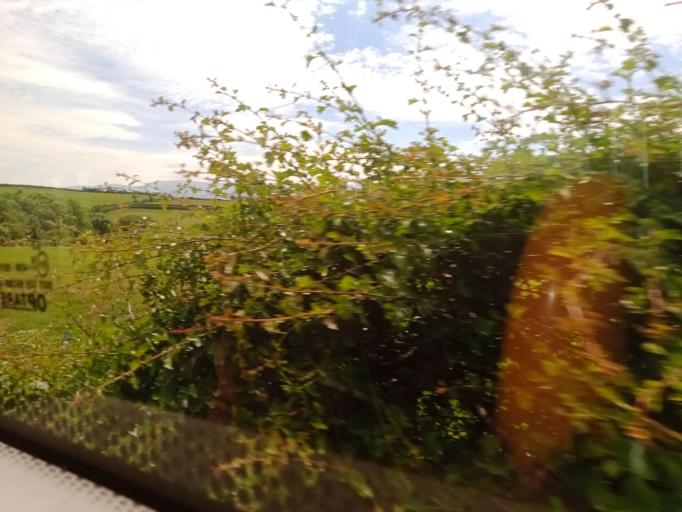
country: GB
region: Wales
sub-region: Anglesey
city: Beaumaris
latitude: 53.2883
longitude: -4.1414
